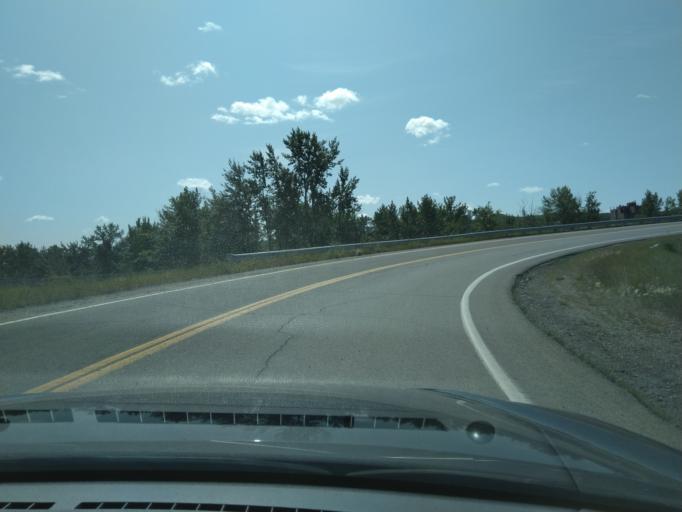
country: CA
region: Alberta
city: Calgary
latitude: 51.1008
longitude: -114.2086
